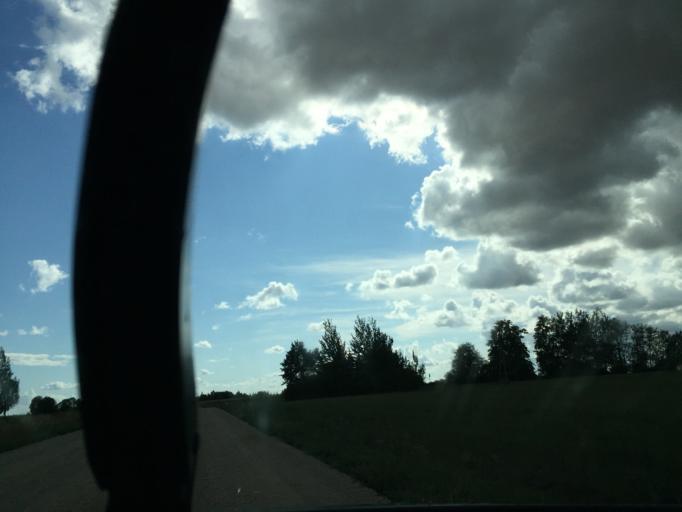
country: LV
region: Tervete
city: Zelmeni
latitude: 56.3007
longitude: 23.4089
